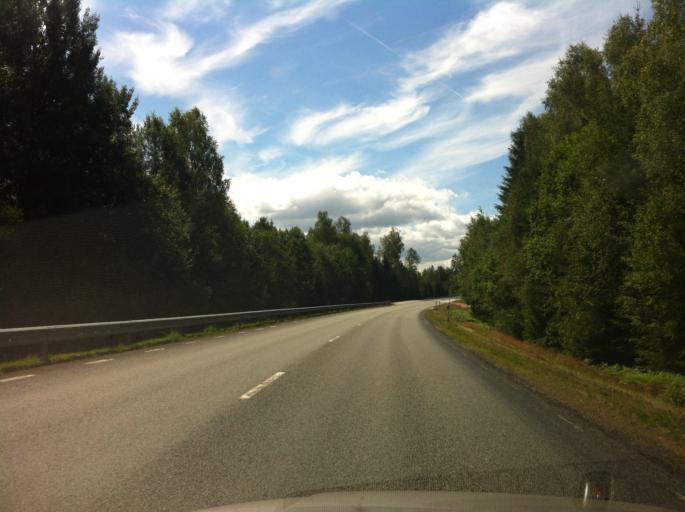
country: SE
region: Joenkoeping
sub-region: Gislaveds Kommun
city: Gislaved
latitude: 57.3804
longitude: 13.5793
